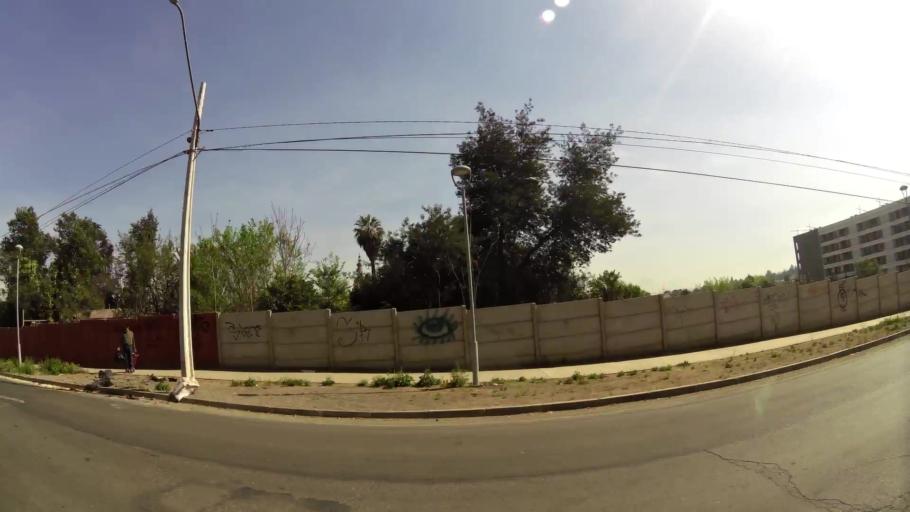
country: CL
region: Santiago Metropolitan
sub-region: Provincia de Santiago
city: Villa Presidente Frei, Nunoa, Santiago, Chile
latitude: -33.5281
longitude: -70.5747
